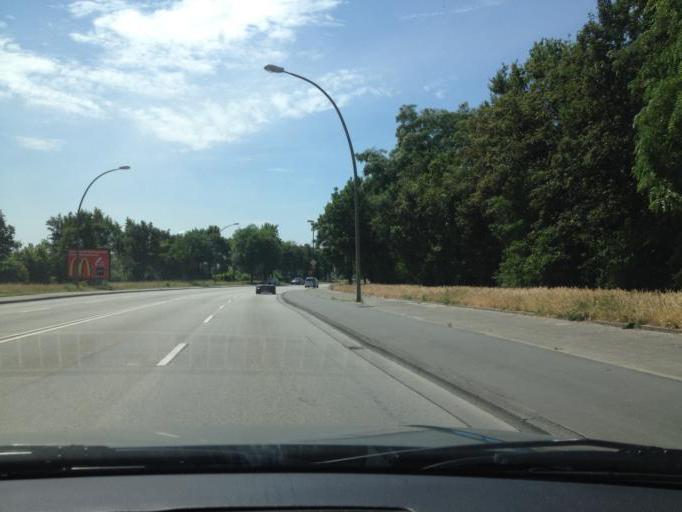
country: DE
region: Rheinland-Pfalz
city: Ludwigshafen am Rhein
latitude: 49.4593
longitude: 8.4352
